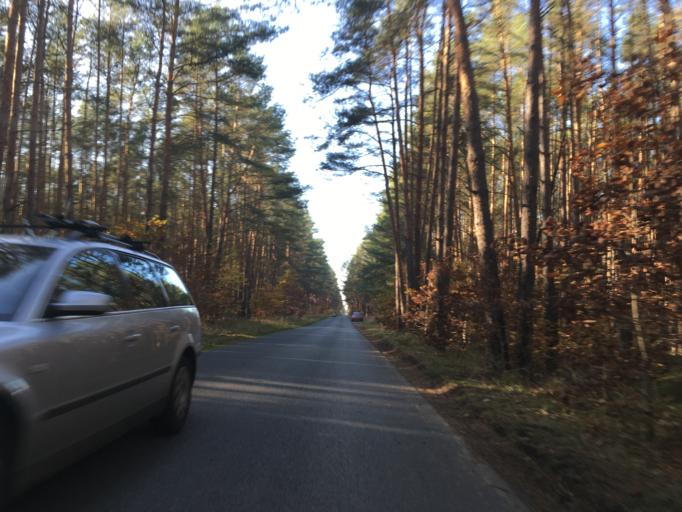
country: DE
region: Brandenburg
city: Spreenhagen
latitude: 52.3432
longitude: 13.9352
